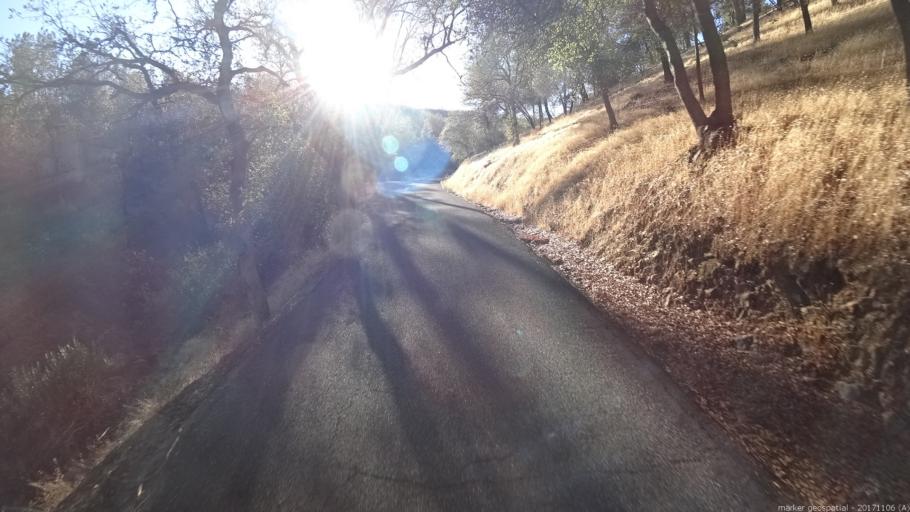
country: US
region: California
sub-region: Shasta County
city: Shasta
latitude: 40.5839
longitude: -122.4873
